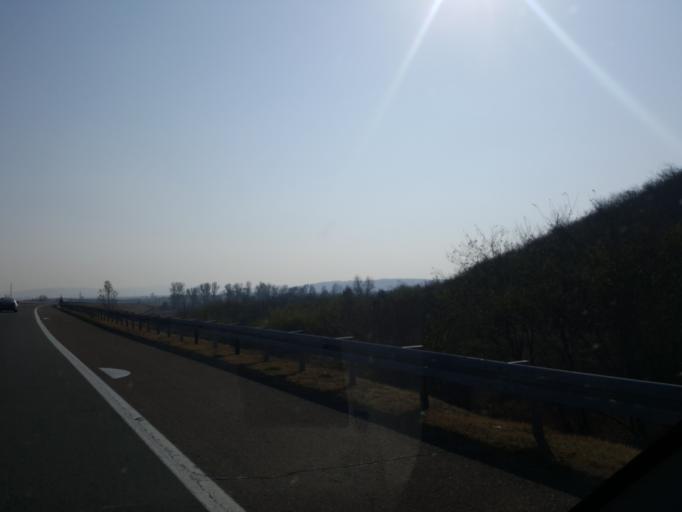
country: RS
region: Central Serbia
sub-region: Nisavski Okrug
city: Doljevac
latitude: 43.2206
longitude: 21.8347
